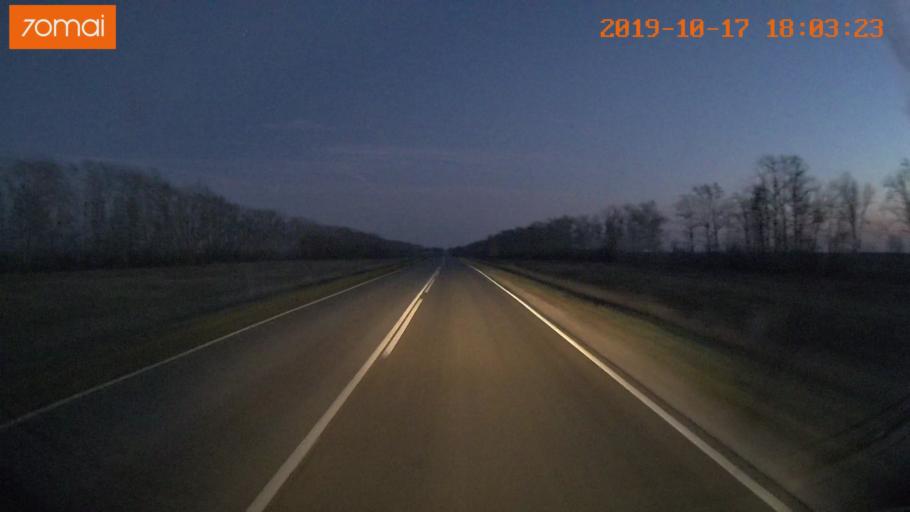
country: RU
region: Tula
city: Kurkino
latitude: 53.4946
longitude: 38.6223
